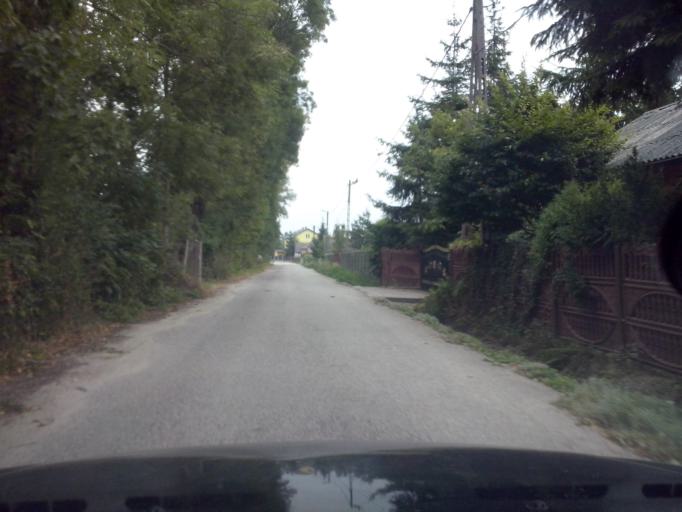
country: PL
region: Swietokrzyskie
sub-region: Powiat kielecki
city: Morawica
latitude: 50.6973
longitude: 20.5771
